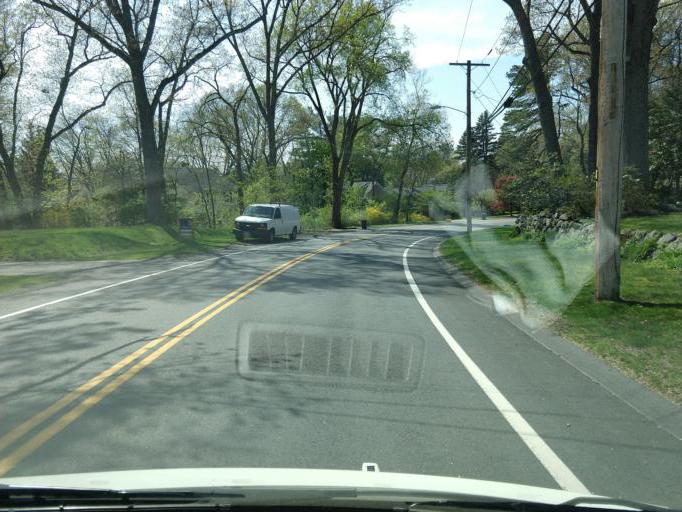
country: US
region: Massachusetts
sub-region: Middlesex County
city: Lexington
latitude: 42.4293
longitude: -71.2140
